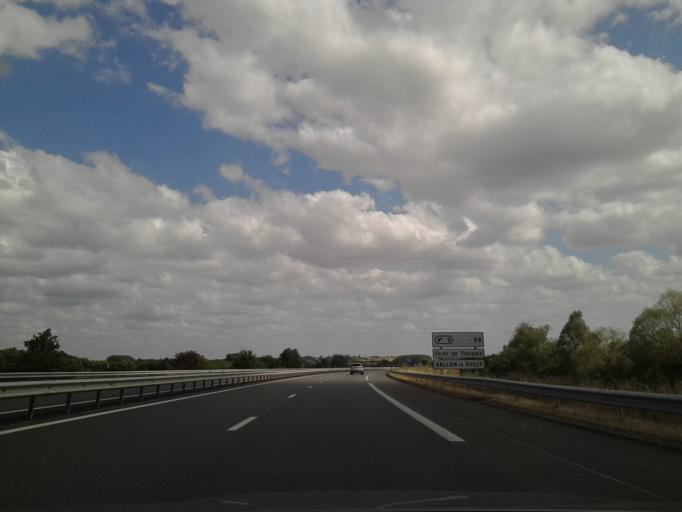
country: FR
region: Centre
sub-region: Departement du Cher
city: Orval
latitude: 46.7153
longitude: 2.4588
